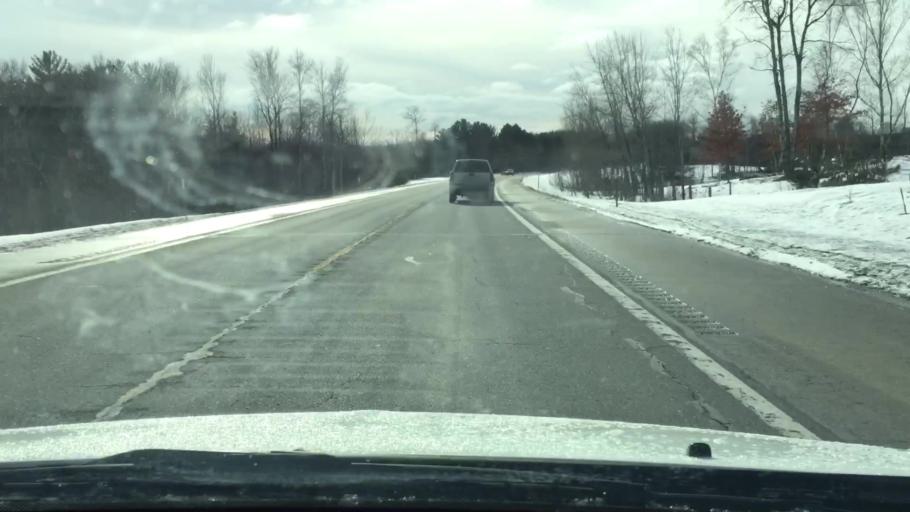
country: US
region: Michigan
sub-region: Wexford County
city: Manton
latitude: 44.5918
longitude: -85.3373
